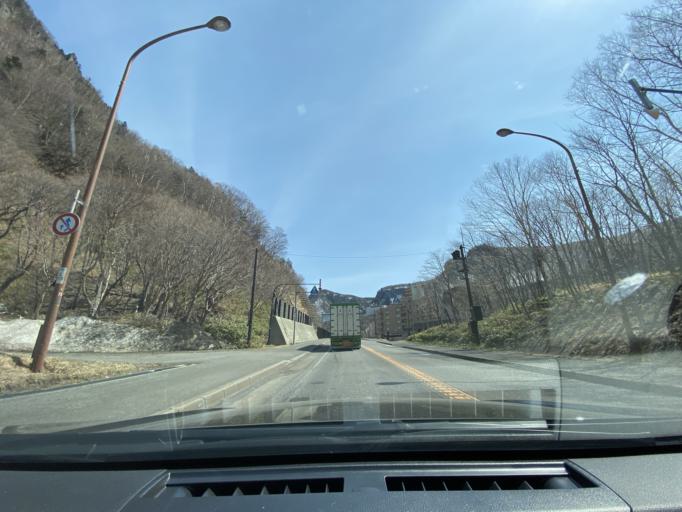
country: JP
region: Hokkaido
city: Kamikawa
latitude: 43.7294
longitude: 142.9438
